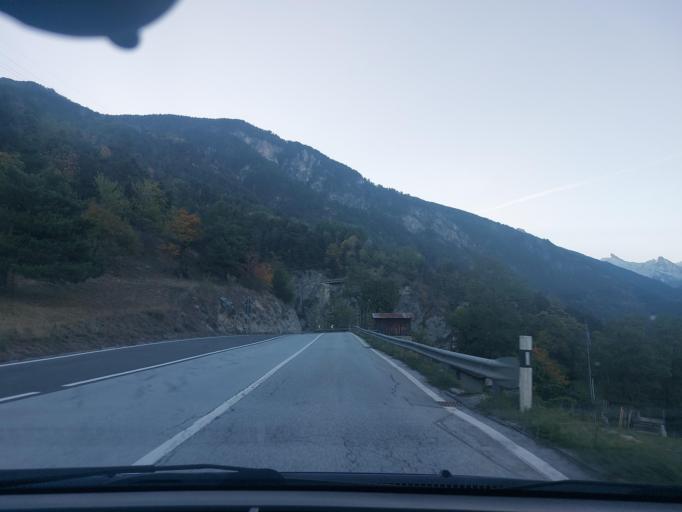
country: CH
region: Valais
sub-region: Sierre District
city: Chippis
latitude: 46.2629
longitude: 7.5603
